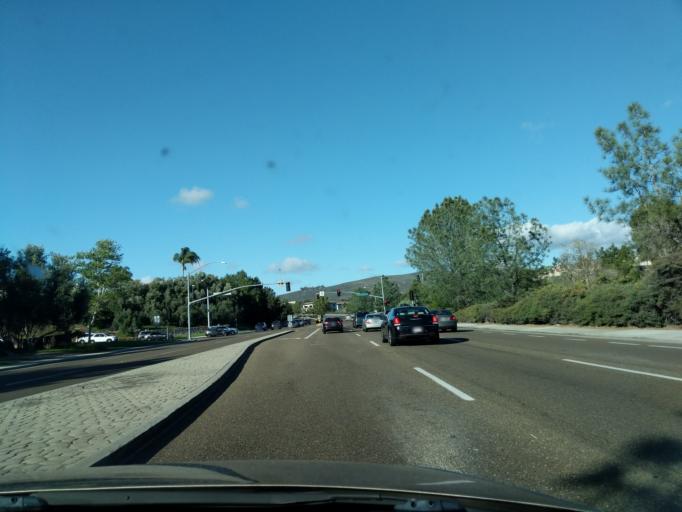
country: US
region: California
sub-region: San Diego County
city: Encinitas
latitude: 33.0716
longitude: -117.2432
